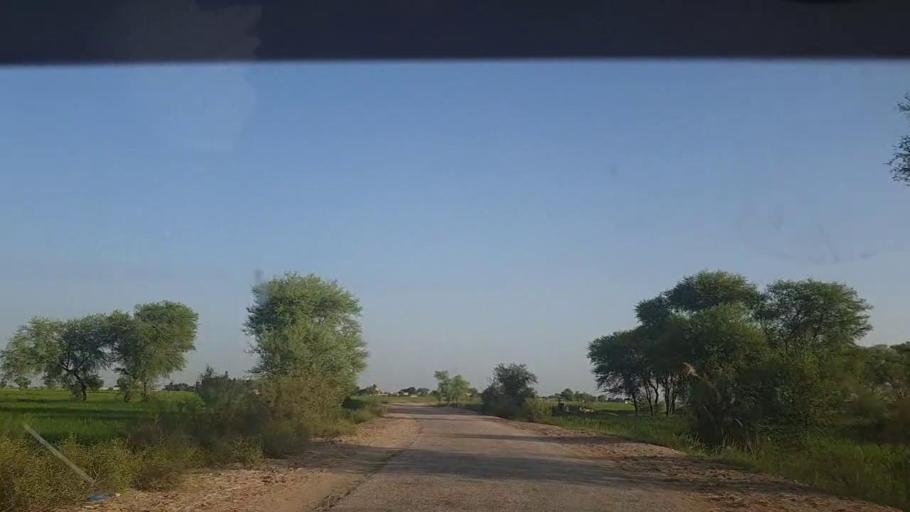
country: PK
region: Sindh
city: Thul
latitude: 28.2042
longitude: 68.8729
